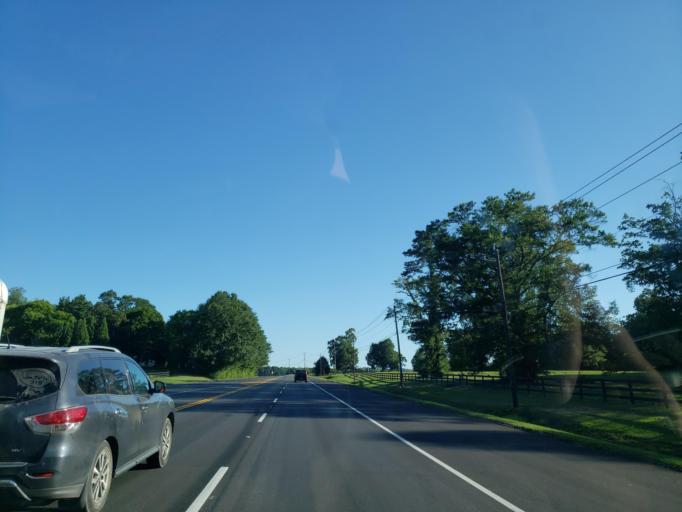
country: US
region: Georgia
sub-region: Floyd County
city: Rome
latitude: 34.2891
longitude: -85.1809
